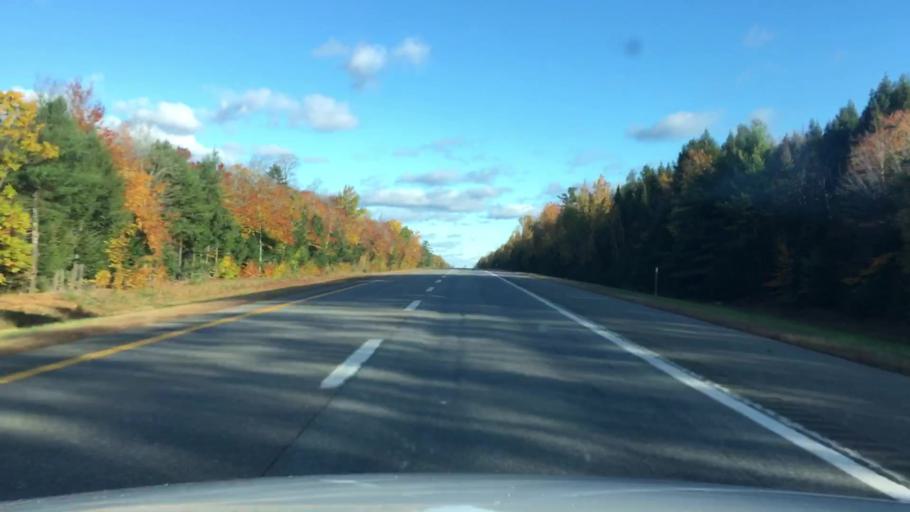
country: US
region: Maine
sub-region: Penobscot County
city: Greenbush
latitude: 45.0673
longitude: -68.6897
